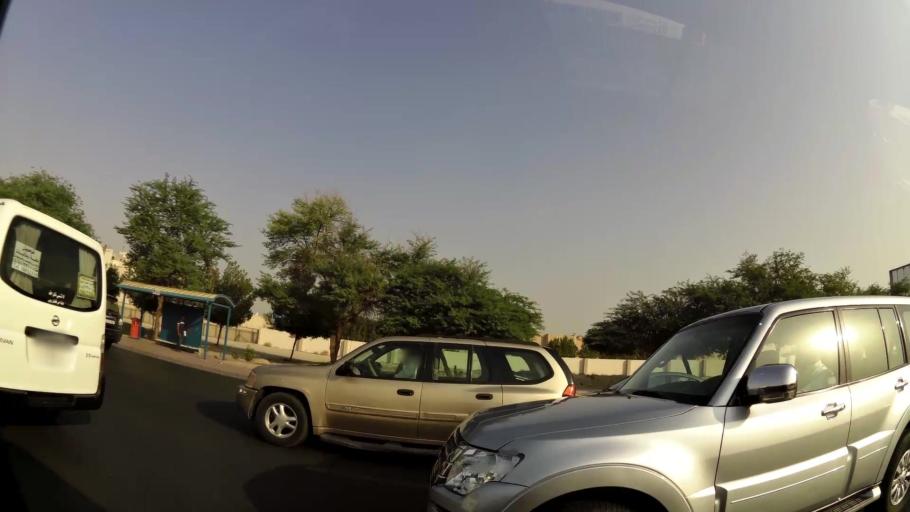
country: KW
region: Al Asimah
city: Ash Shamiyah
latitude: 29.3167
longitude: 47.9572
